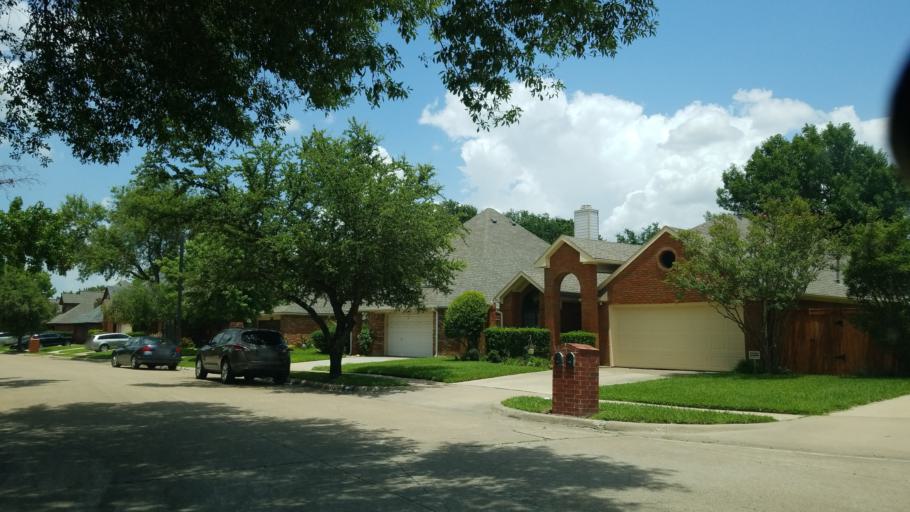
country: US
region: Texas
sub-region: Dallas County
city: Farmers Branch
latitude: 32.9364
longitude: -96.9528
